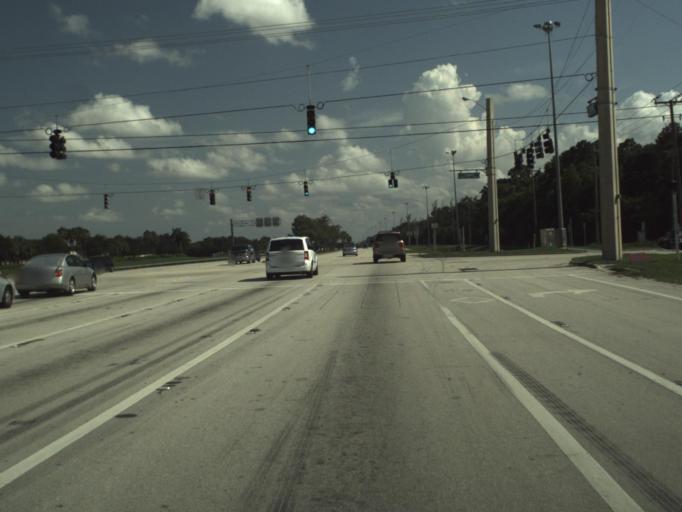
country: US
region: Florida
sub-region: Palm Beach County
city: Wellington
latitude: 26.5920
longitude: -80.2060
